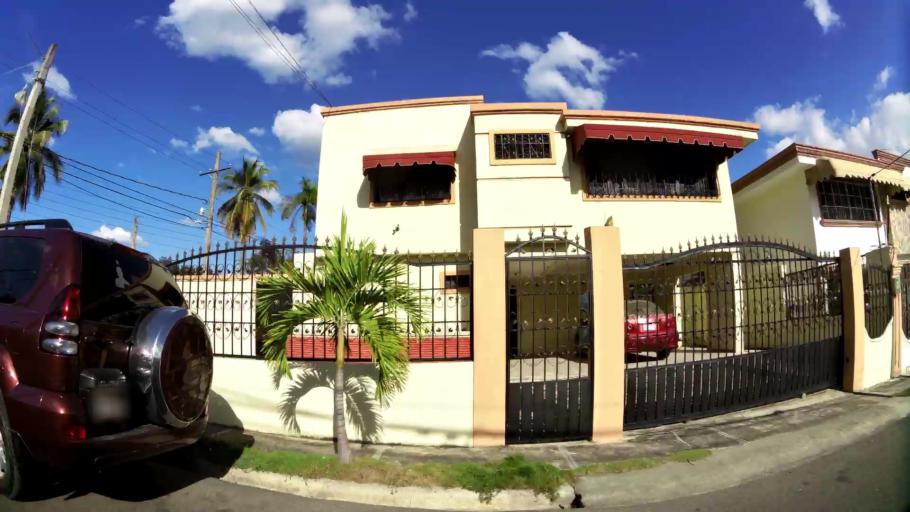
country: DO
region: Nacional
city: Santo Domingo
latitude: 18.5058
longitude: -69.9828
